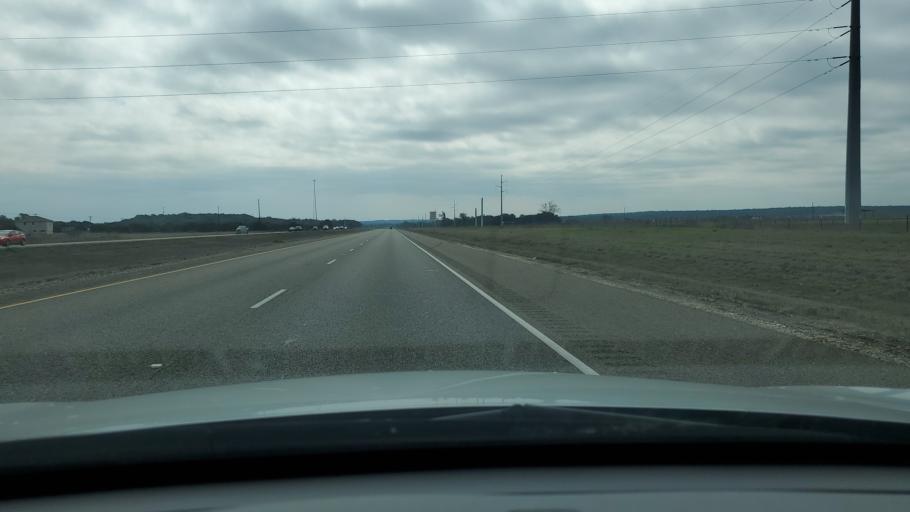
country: US
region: Texas
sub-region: Williamson County
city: Florence
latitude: 30.7852
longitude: -97.7638
